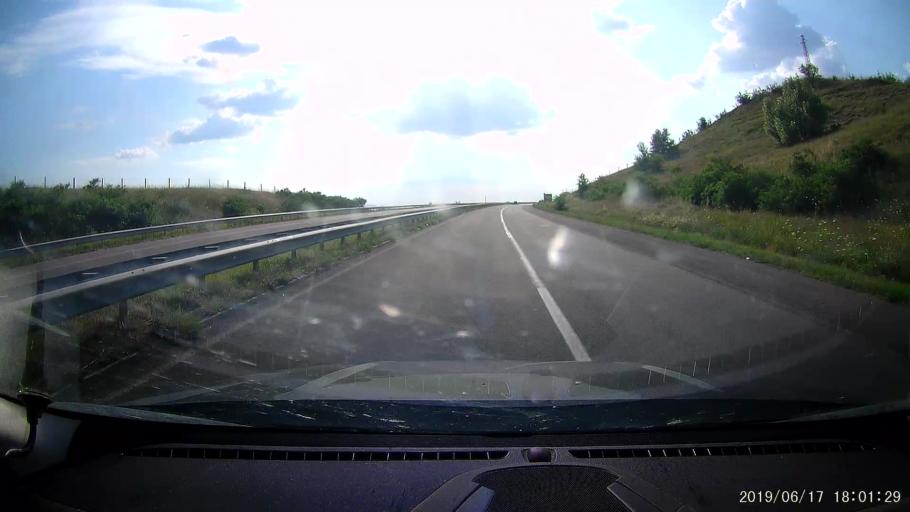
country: BG
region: Khaskovo
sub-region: Obshtina Svilengrad
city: Svilengrad
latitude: 41.7459
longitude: 26.2531
